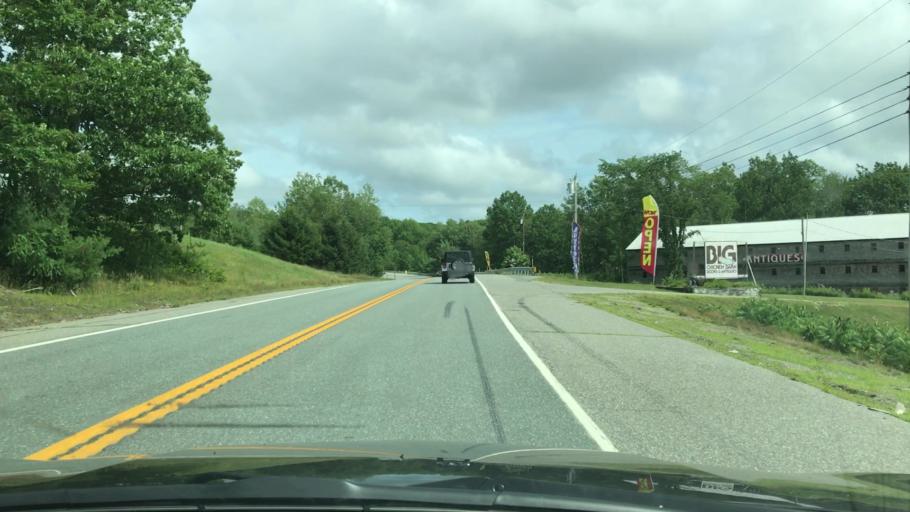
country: US
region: Maine
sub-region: Hancock County
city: Surry
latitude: 44.5626
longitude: -68.5876
